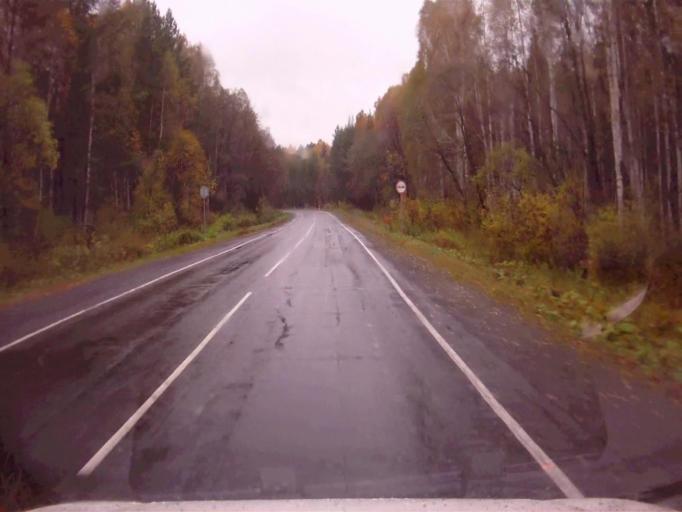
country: RU
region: Chelyabinsk
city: Verkhniy Ufaley
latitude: 55.9564
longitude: 60.3907
